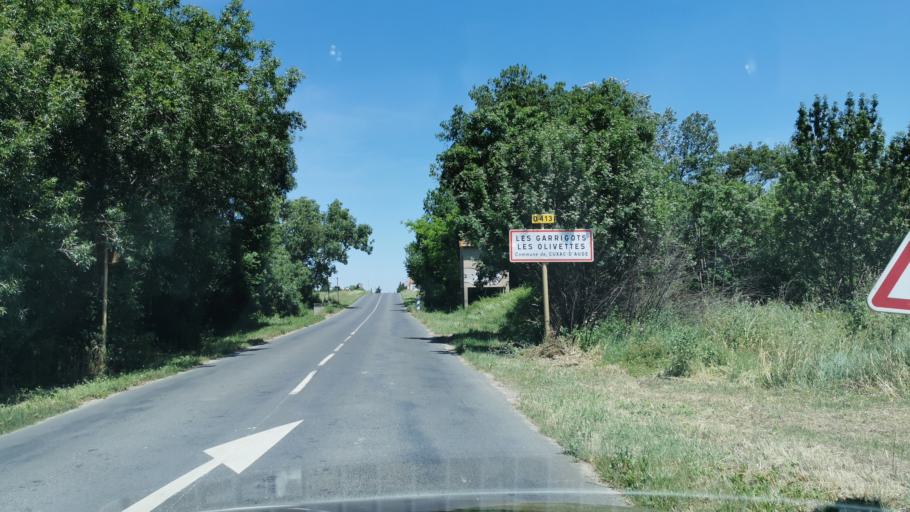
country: FR
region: Languedoc-Roussillon
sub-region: Departement de l'Aude
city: Ouveillan
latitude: 43.2585
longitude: 3.0072
